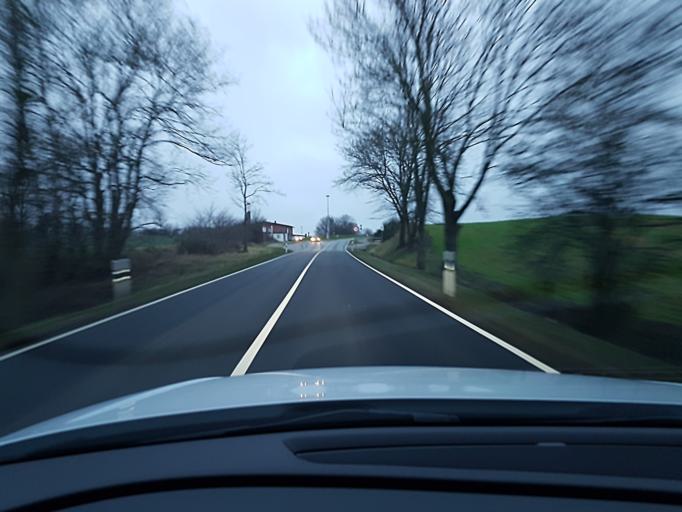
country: DE
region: Mecklenburg-Vorpommern
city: Satow-Oberhagen
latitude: 53.9741
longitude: 11.8682
